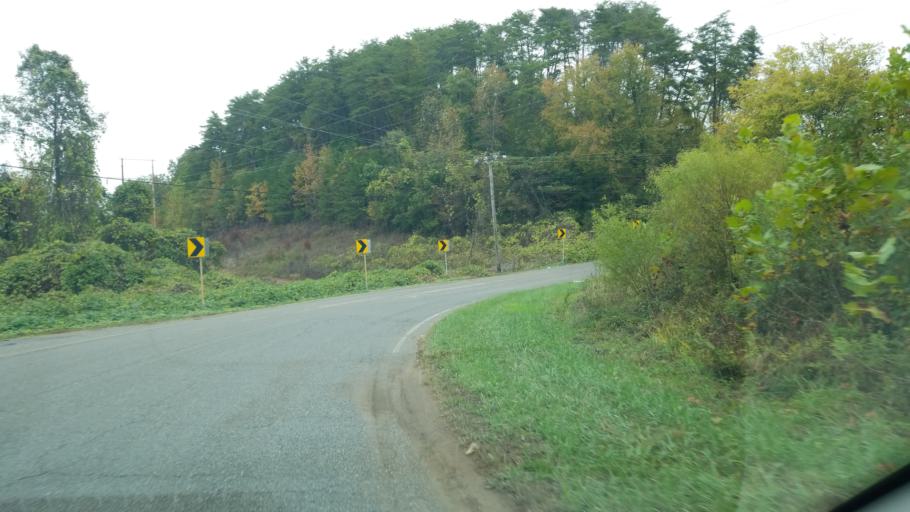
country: US
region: Tennessee
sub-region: Rhea County
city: Dayton
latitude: 35.5127
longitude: -85.0221
